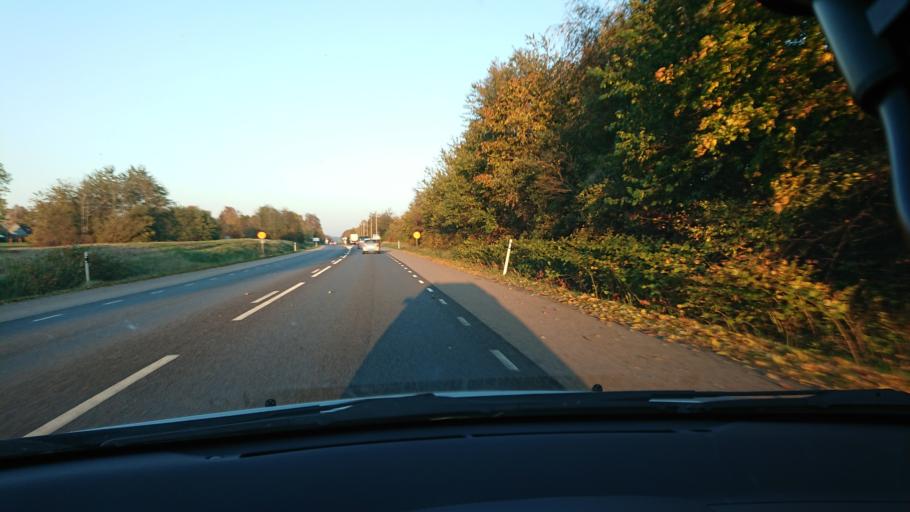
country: SE
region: Halland
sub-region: Halmstads Kommun
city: Fyllinge
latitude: 56.6780
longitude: 12.9251
